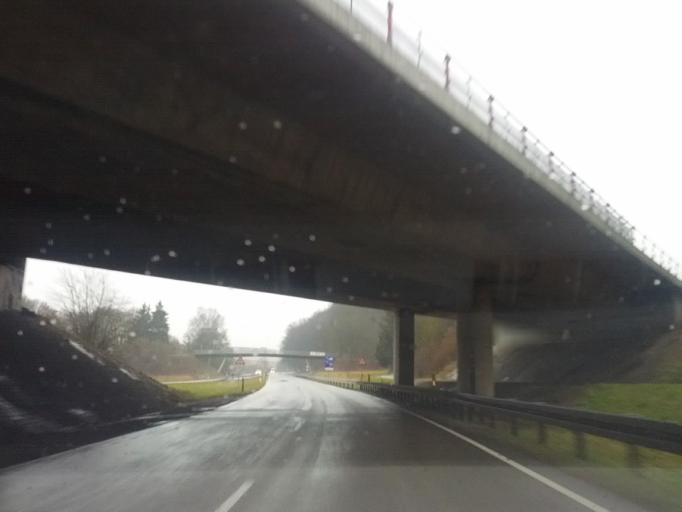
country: DE
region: Baden-Wuerttemberg
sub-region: Tuebingen Region
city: Ummendorf
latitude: 48.0800
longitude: 9.8159
